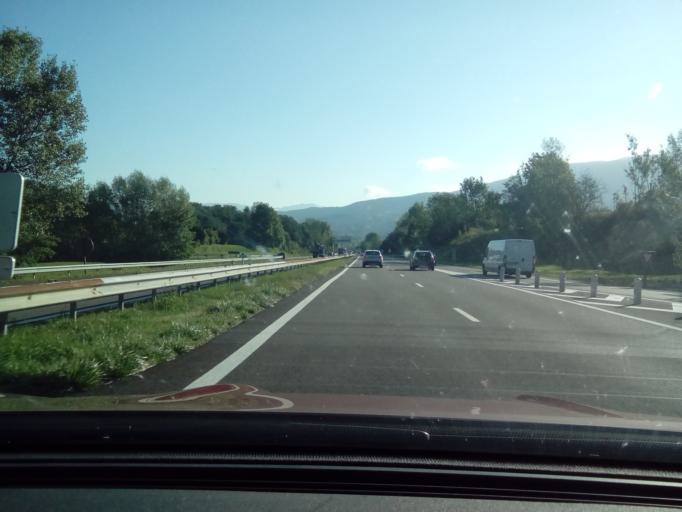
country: FR
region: Rhone-Alpes
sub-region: Departement de la Haute-Savoie
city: Alby-sur-Cheran
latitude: 45.8180
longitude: 6.0095
